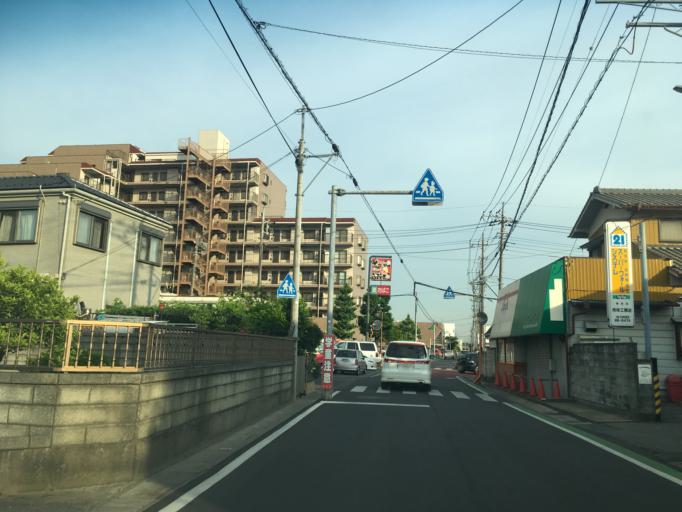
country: JP
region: Saitama
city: Yoshikawa
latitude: 35.8651
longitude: 139.8191
